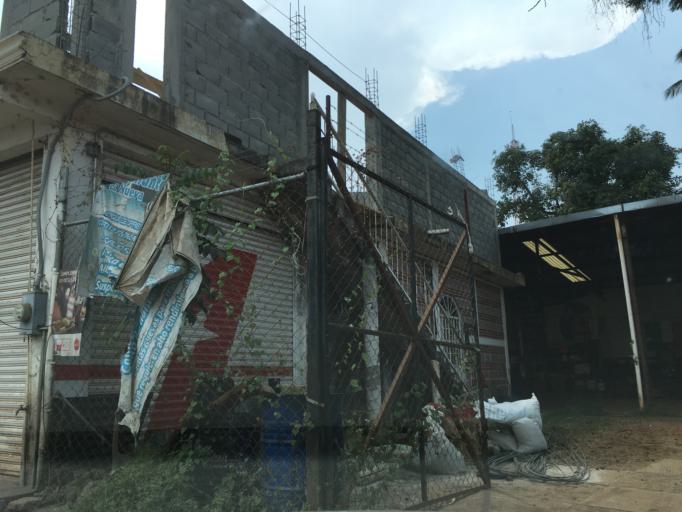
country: MX
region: Michoacan
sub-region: Ziracuaretiro
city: Patuan
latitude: 19.4175
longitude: -101.9148
